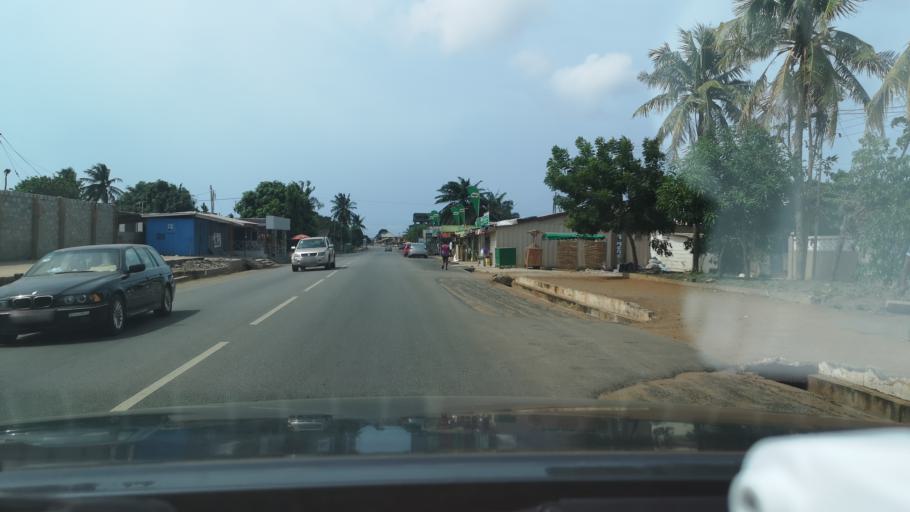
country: GH
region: Greater Accra
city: Tema
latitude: 5.6669
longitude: -0.0292
